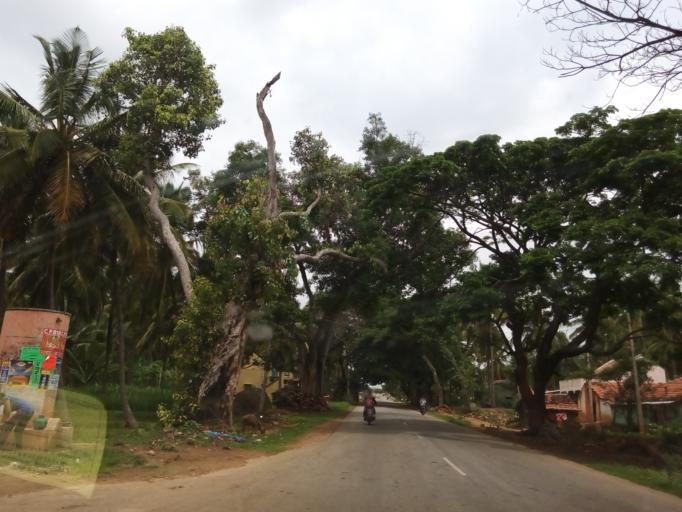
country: IN
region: Karnataka
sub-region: Hassan
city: Shravanabelagola
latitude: 12.8715
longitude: 76.4506
